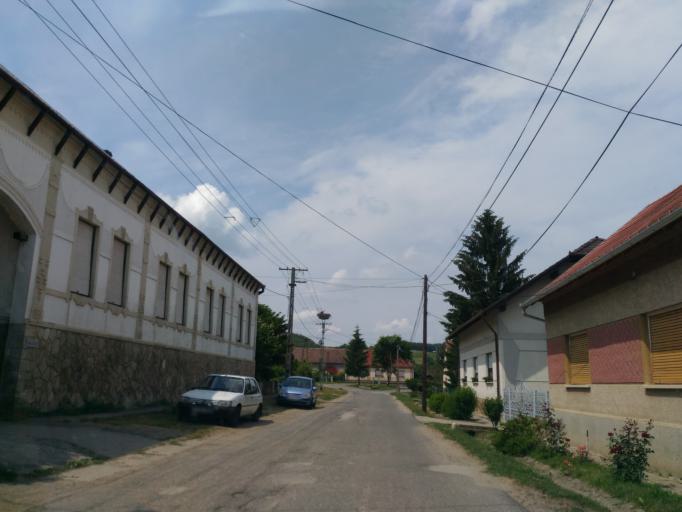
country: HU
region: Baranya
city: Komlo
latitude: 46.1963
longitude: 18.2268
